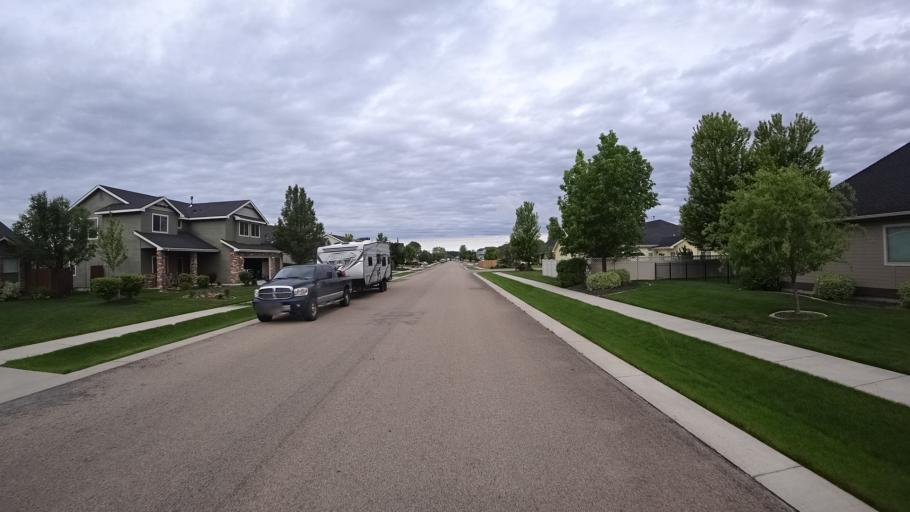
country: US
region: Idaho
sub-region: Ada County
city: Star
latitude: 43.6962
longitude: -116.5039
